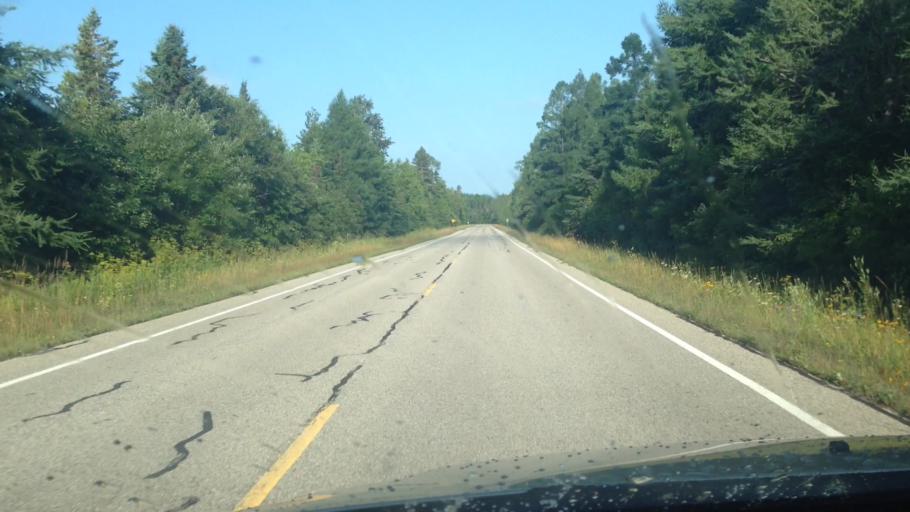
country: US
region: Michigan
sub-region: Mackinac County
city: Saint Ignace
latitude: 45.8930
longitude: -84.7779
